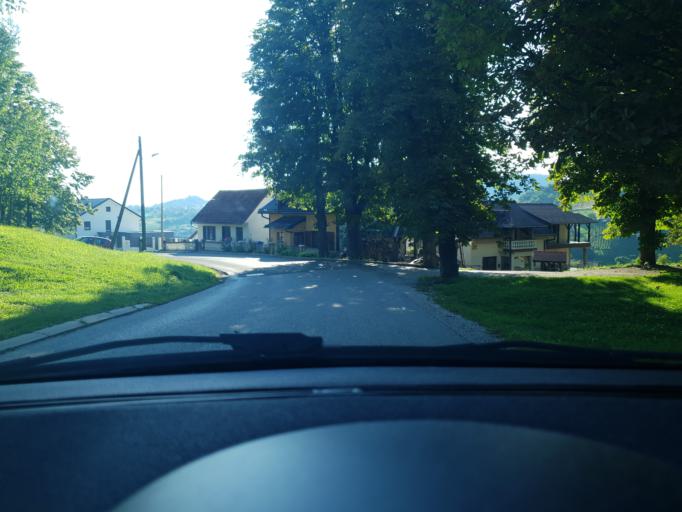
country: HR
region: Krapinsko-Zagorska
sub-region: Grad Krapina
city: Krapina
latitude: 46.1638
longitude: 15.8819
